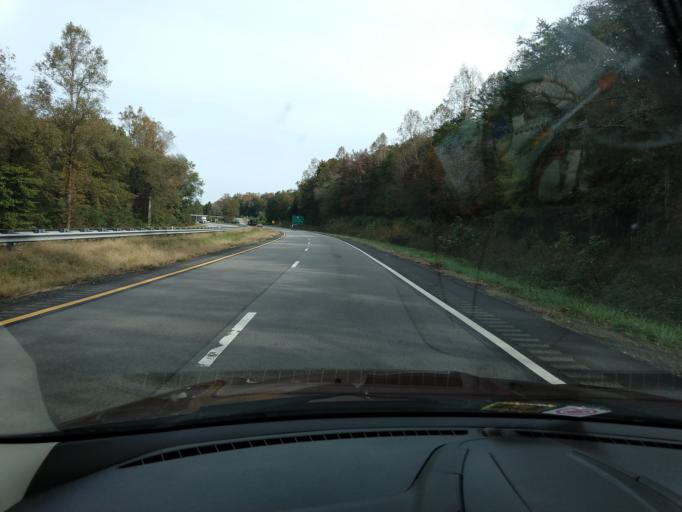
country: US
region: Virginia
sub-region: Pittsylvania County
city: Chatham
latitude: 36.8220
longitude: -79.3812
